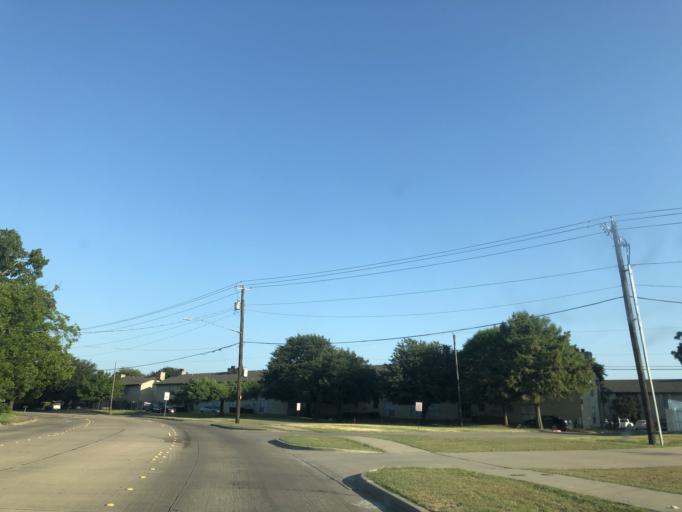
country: US
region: Texas
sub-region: Dallas County
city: Sunnyvale
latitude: 32.8481
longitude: -96.5612
